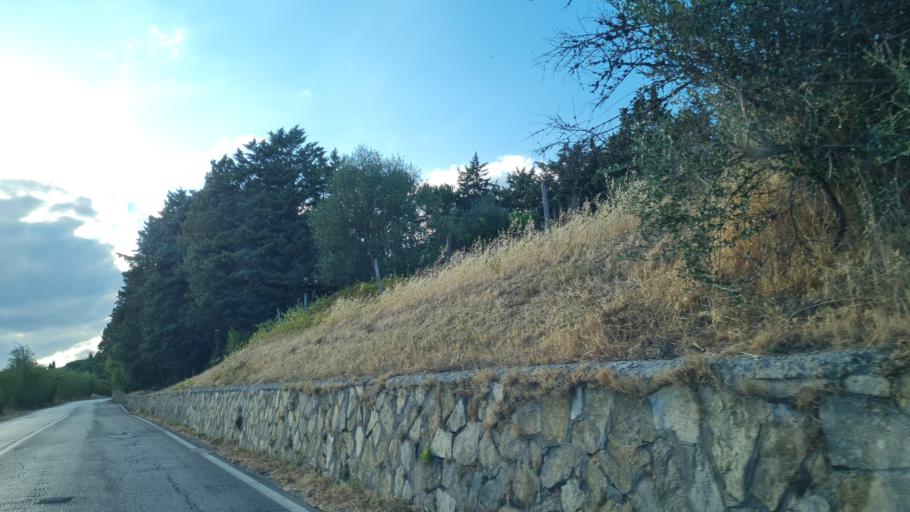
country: IT
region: Tuscany
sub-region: Provincia di Siena
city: Chianciano Terme
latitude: 43.0341
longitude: 11.8460
